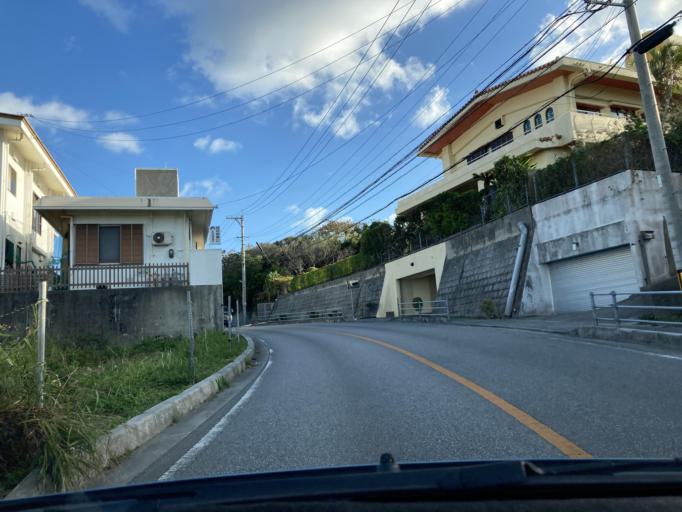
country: JP
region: Okinawa
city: Chatan
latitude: 26.2972
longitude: 127.7989
